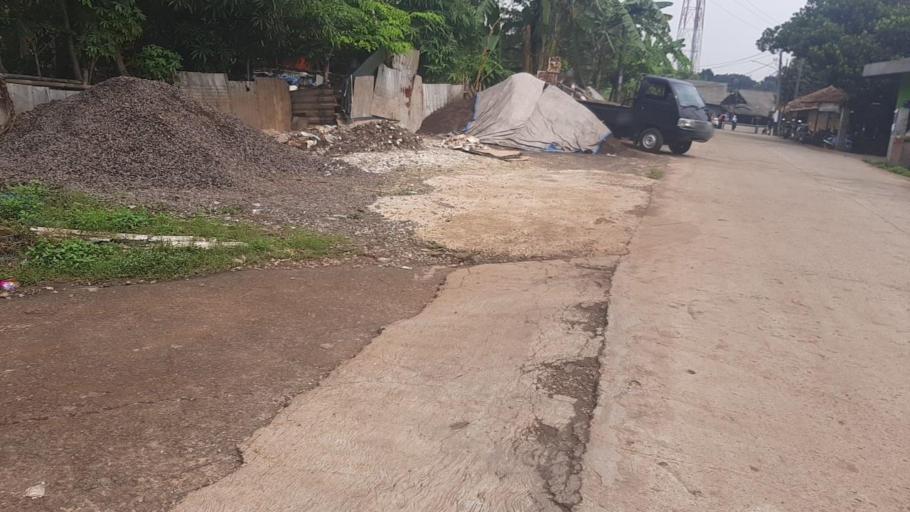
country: ID
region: West Java
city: Cileungsir
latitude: -6.4203
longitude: 106.9453
